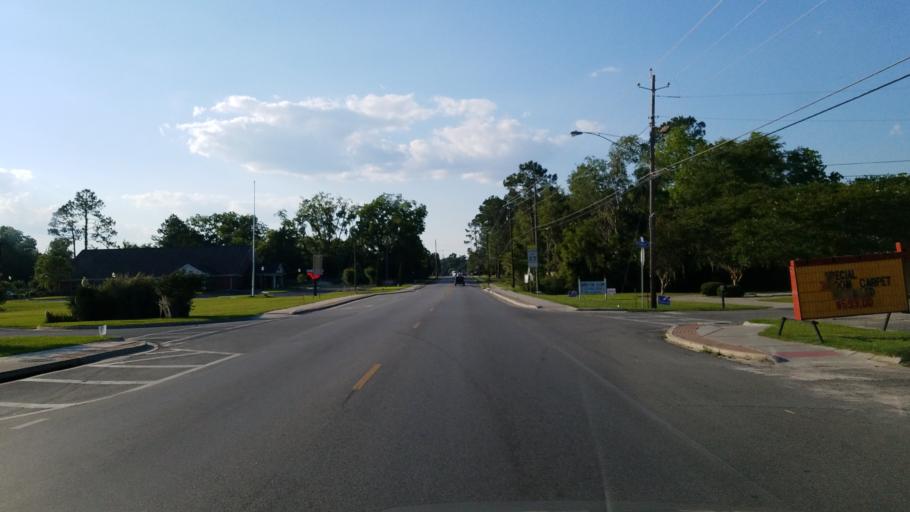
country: US
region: Georgia
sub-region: Lanier County
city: Lakeland
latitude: 31.0359
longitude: -83.0734
